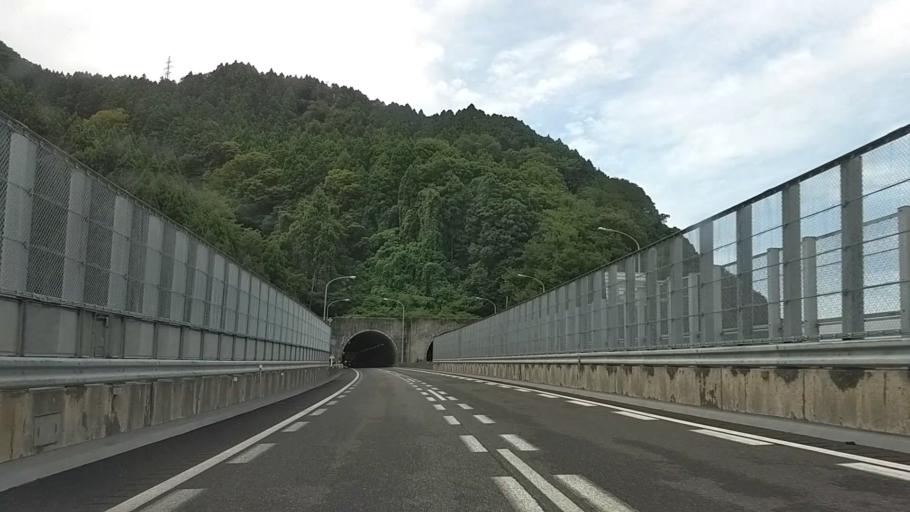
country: JP
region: Niigata
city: Itoigawa
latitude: 36.9972
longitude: 137.7092
